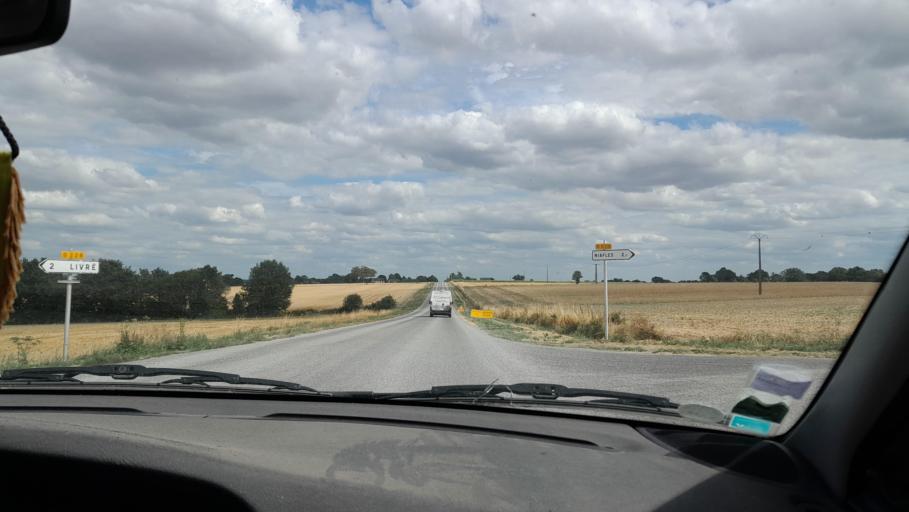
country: FR
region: Pays de la Loire
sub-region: Departement de la Mayenne
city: Craon
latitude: 47.8674
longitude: -0.9926
